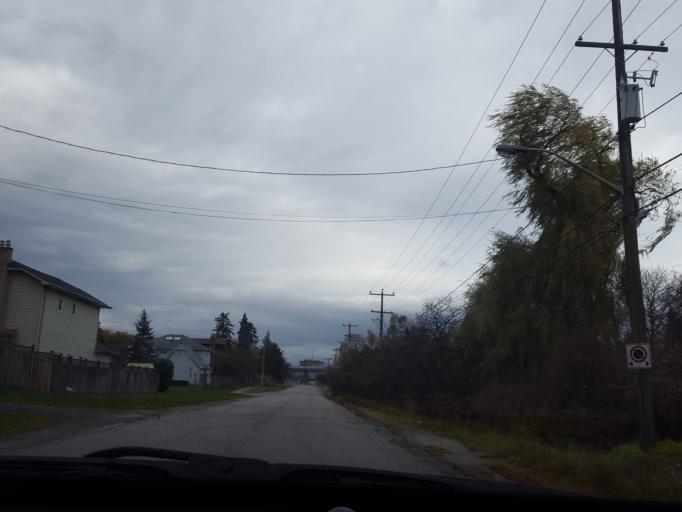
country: CA
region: Ontario
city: Ajax
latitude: 43.8220
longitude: -79.0735
